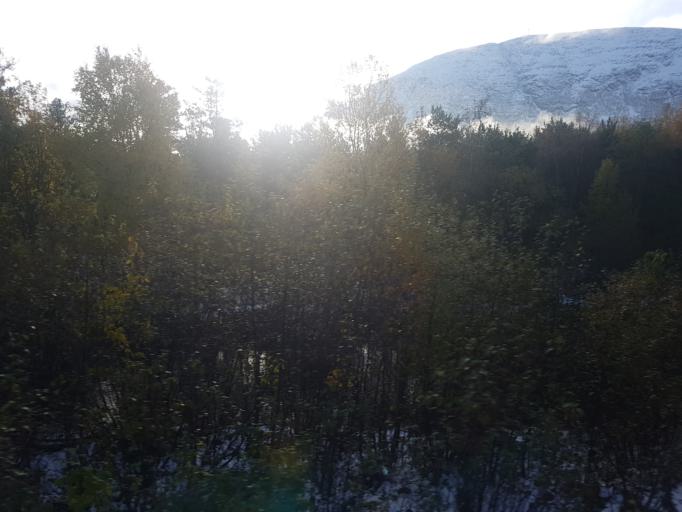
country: NO
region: Sor-Trondelag
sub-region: Oppdal
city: Oppdal
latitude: 62.5970
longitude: 9.6744
